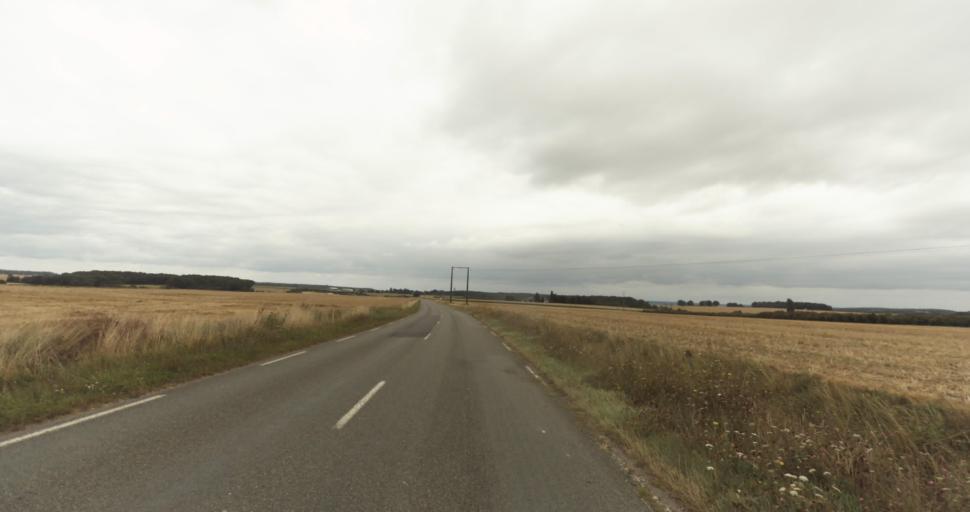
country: FR
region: Haute-Normandie
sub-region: Departement de l'Eure
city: Gravigny
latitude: 49.0536
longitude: 1.2385
